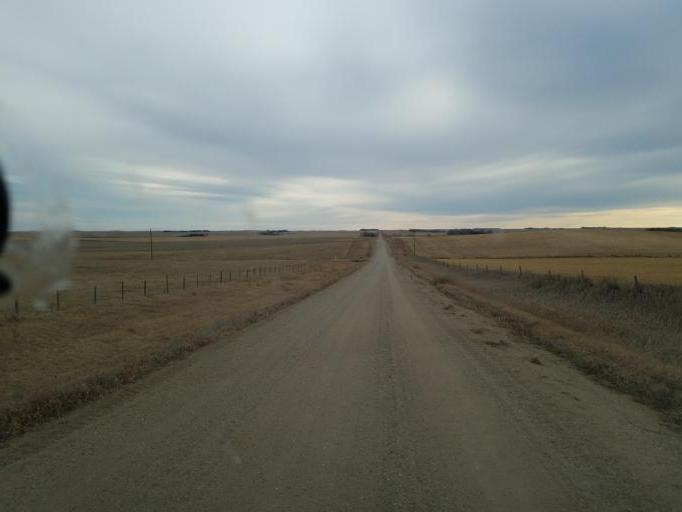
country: US
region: Nebraska
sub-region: Knox County
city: Bloomfield
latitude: 42.5250
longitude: -97.7371
